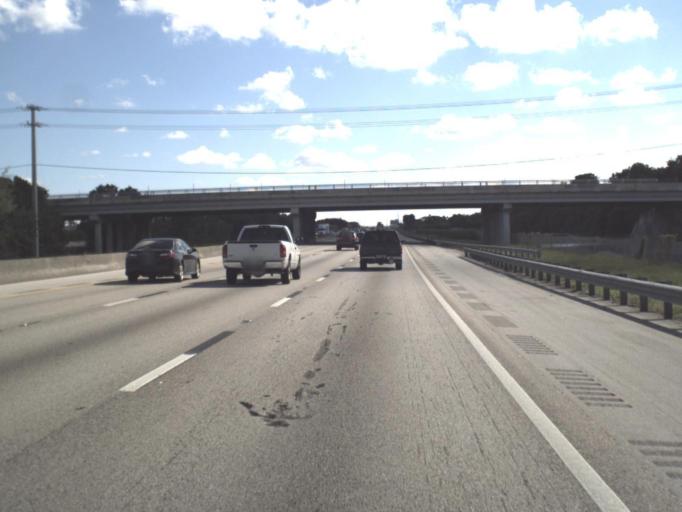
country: US
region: Florida
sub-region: Palm Beach County
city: Boca Pointe
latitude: 26.3329
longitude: -80.1705
